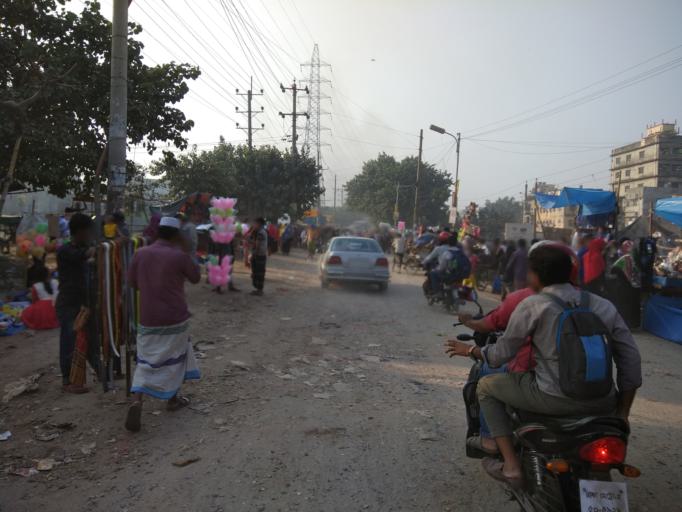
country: BD
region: Dhaka
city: Azimpur
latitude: 23.7205
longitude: 90.3777
